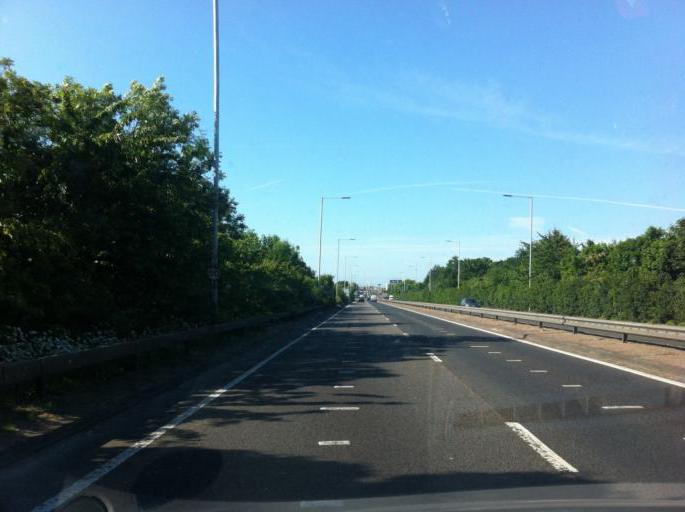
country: GB
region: England
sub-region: Greater London
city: Hayes
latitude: 51.5103
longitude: -0.4035
